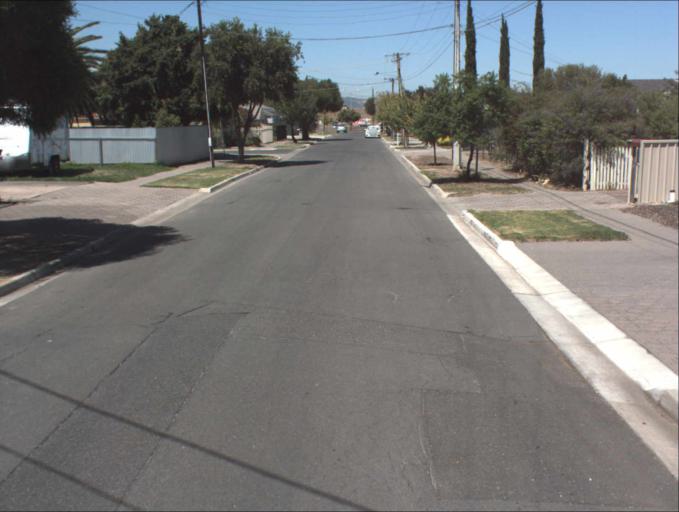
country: AU
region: South Australia
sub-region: Port Adelaide Enfield
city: Klemzig
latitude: -34.8677
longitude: 138.6350
